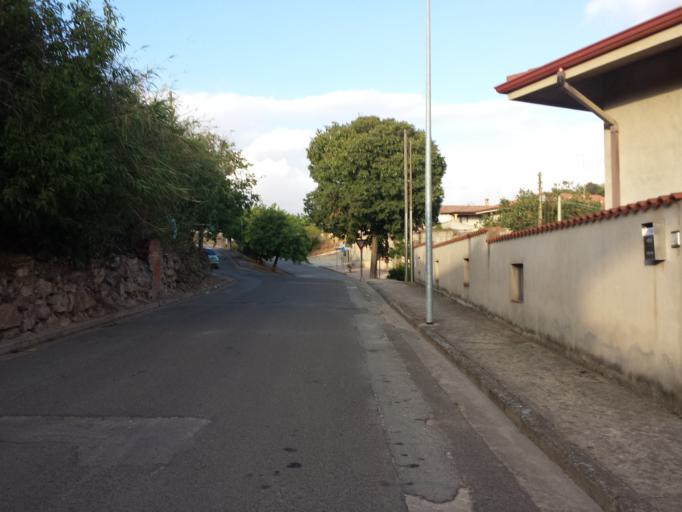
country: IT
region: Sardinia
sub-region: Provincia di Medio Campidano
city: Serrenti
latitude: 39.4955
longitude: 8.9838
